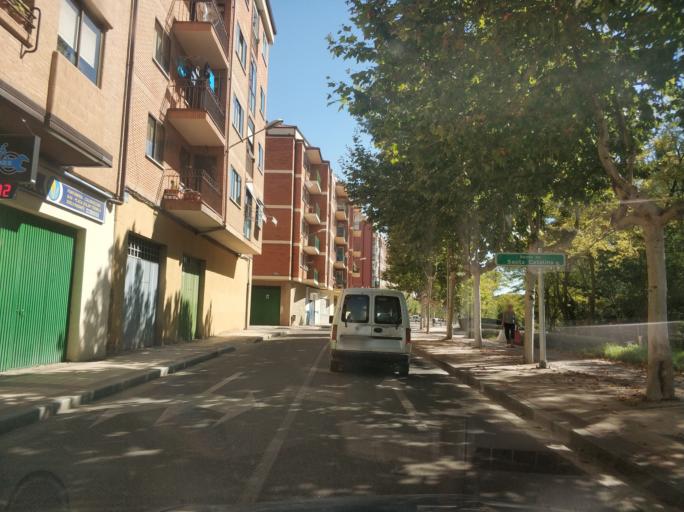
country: ES
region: Castille and Leon
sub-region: Provincia de Burgos
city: Aranda de Duero
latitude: 41.6693
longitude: -3.6815
